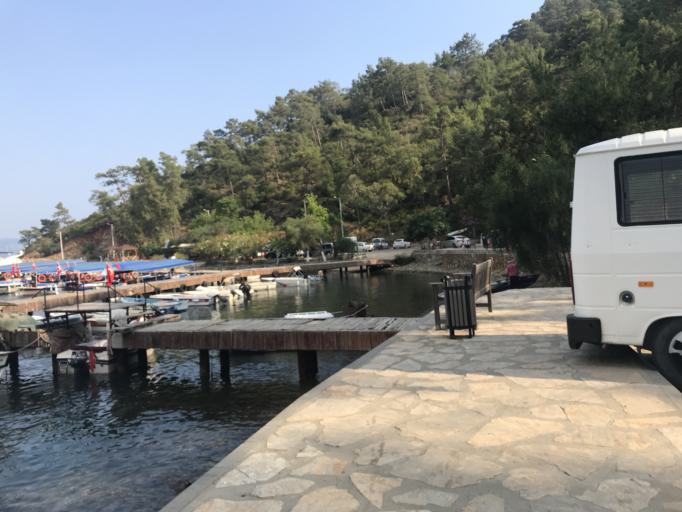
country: TR
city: Dalyan
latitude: 36.8289
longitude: 28.5483
